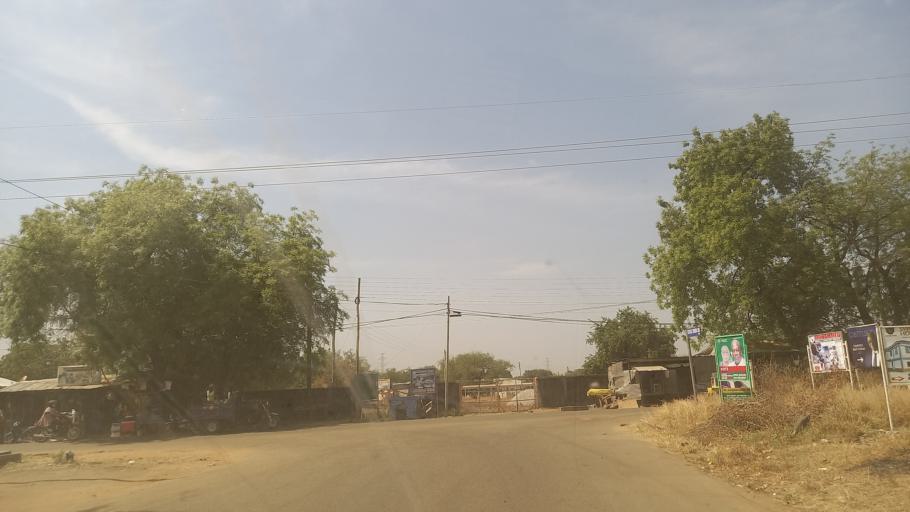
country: GH
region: Upper East
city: Navrongo
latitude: 10.8821
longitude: -1.0840
